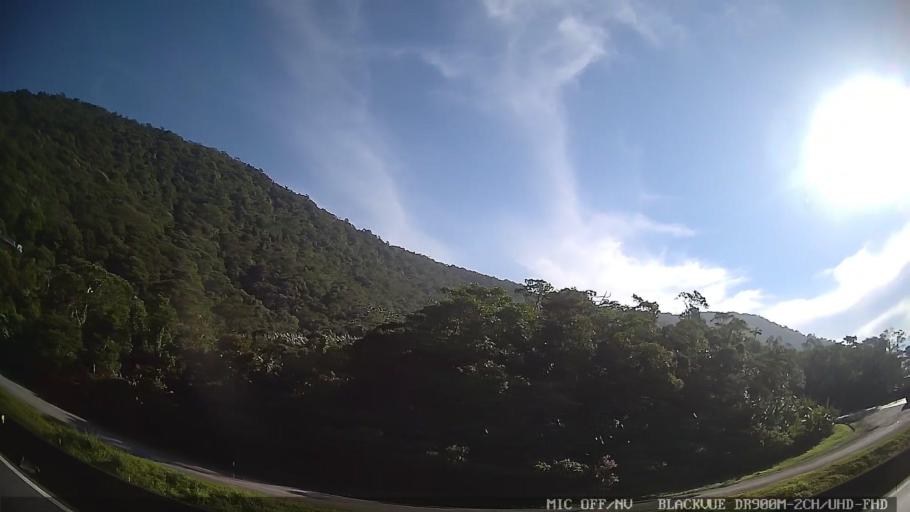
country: BR
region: Sao Paulo
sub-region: Cubatao
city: Cubatao
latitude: -23.8869
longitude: -46.4783
